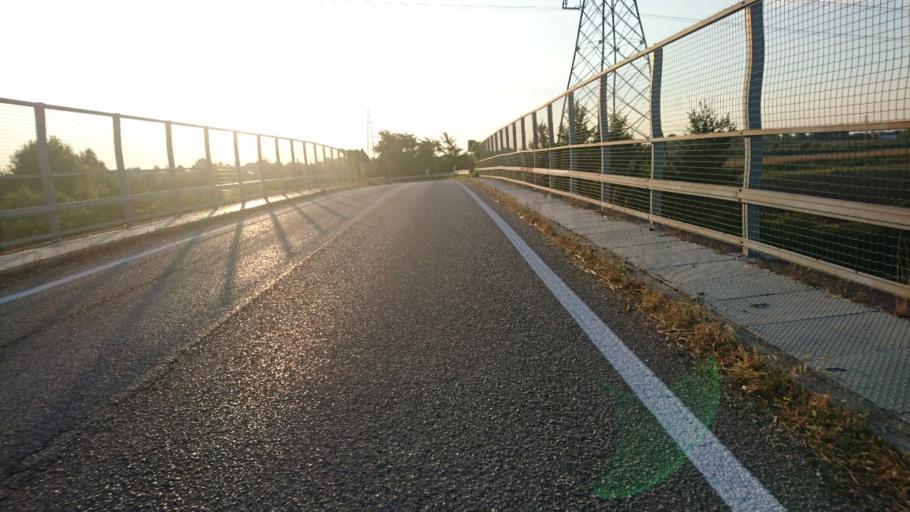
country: IT
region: Veneto
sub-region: Provincia di Padova
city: Ponte San Nicolo
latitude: 45.3688
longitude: 11.9484
